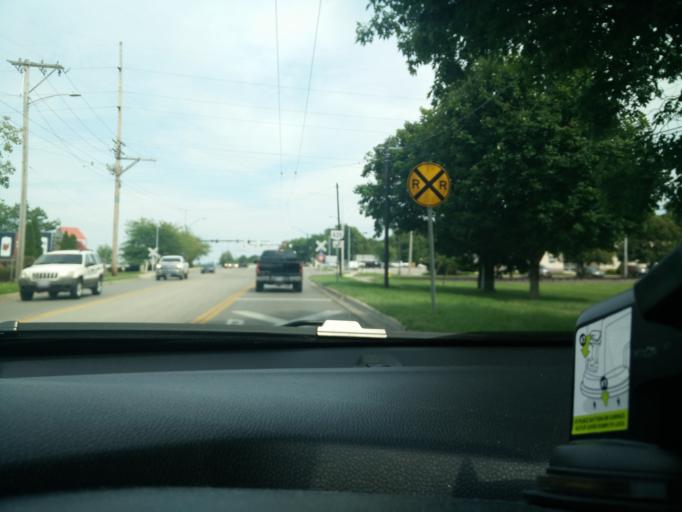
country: US
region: Ohio
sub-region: Montgomery County
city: Oakwood
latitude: 39.7226
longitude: -84.1248
